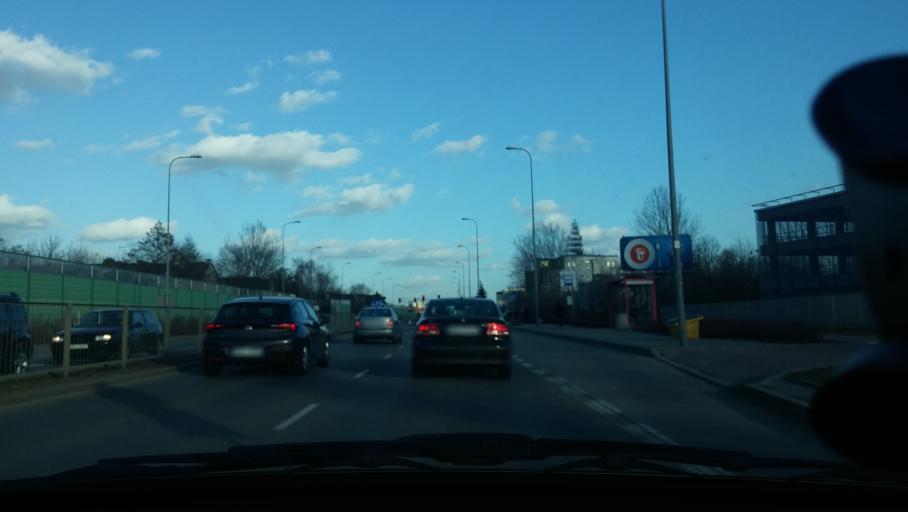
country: PL
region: Masovian Voivodeship
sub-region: Warszawa
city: Ursynow
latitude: 52.1546
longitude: 21.0073
